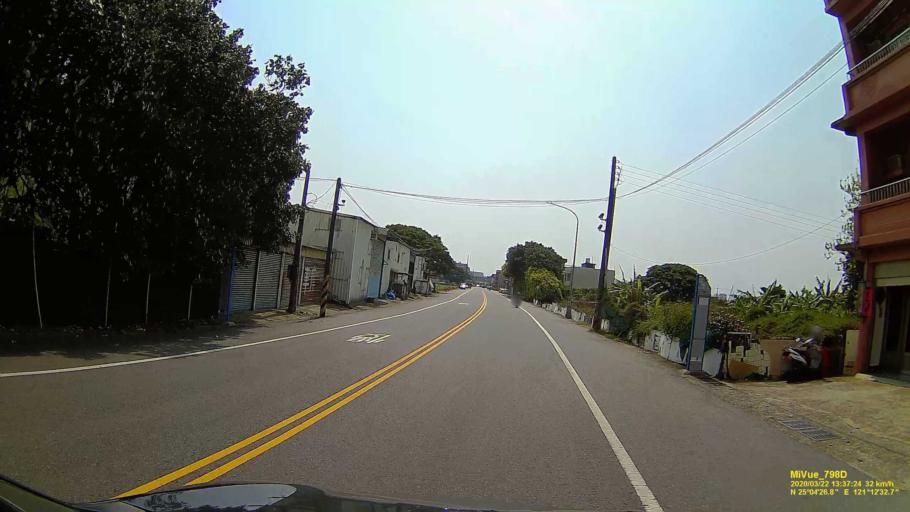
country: TW
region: Taiwan
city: Taoyuan City
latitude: 25.0740
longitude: 121.2089
